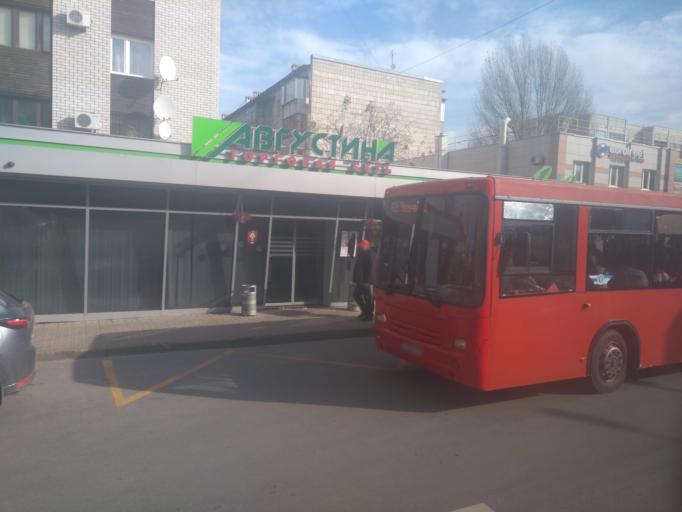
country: RU
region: Tatarstan
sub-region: Gorod Kazan'
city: Kazan
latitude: 55.7986
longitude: 49.1918
